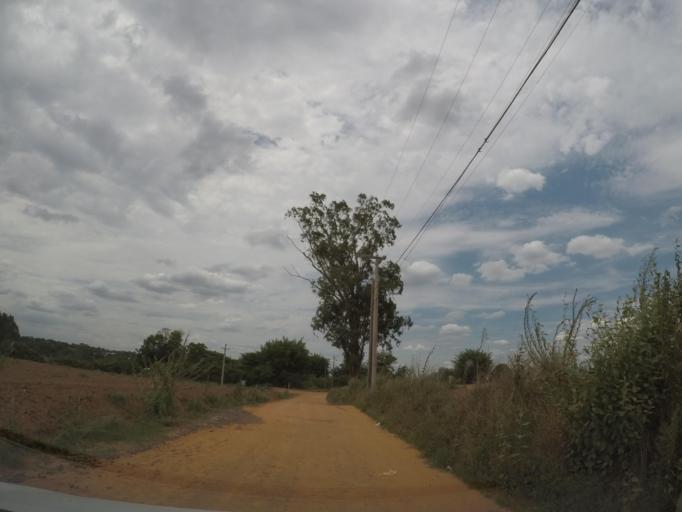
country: BR
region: Sao Paulo
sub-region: Sumare
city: Sumare
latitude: -22.8358
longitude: -47.2910
